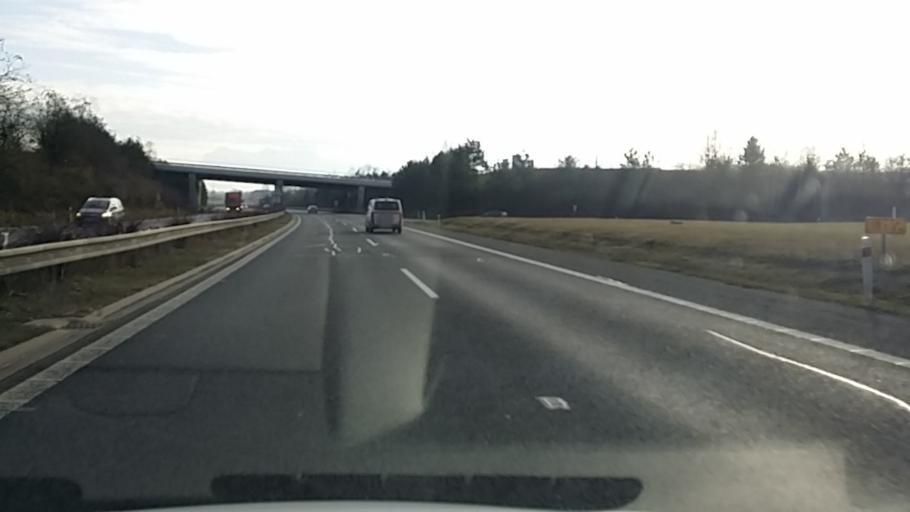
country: CZ
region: Central Bohemia
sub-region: Okres Melnik
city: Veltrusy
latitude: 50.3126
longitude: 14.3146
